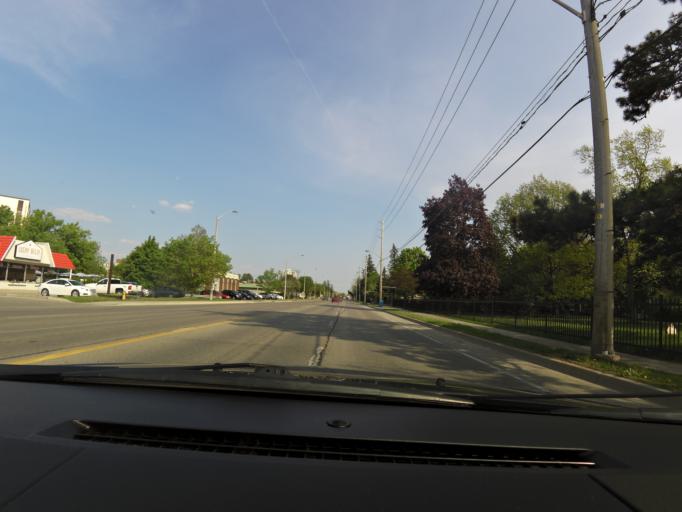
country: CA
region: Ontario
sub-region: Wellington County
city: Guelph
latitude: 43.5645
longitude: -80.2767
